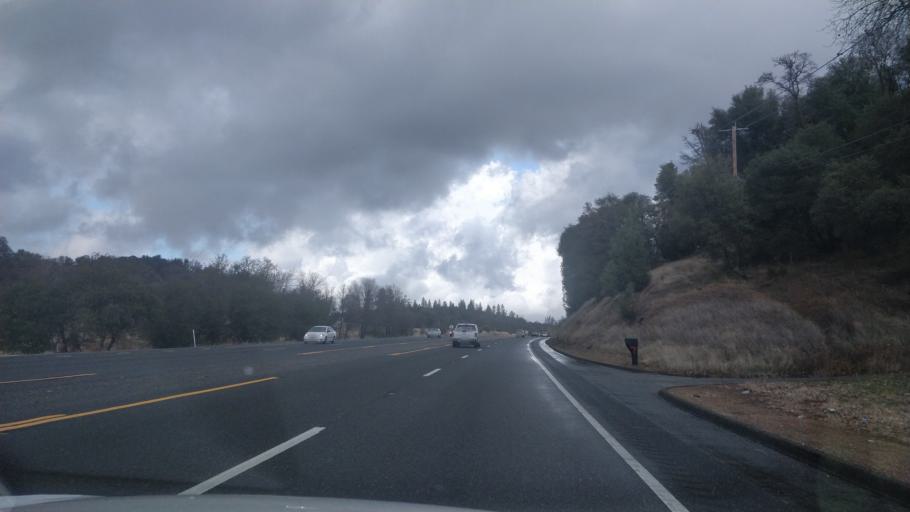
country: US
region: California
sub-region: Nevada County
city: Lake of the Pines
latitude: 39.0257
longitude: -121.0989
